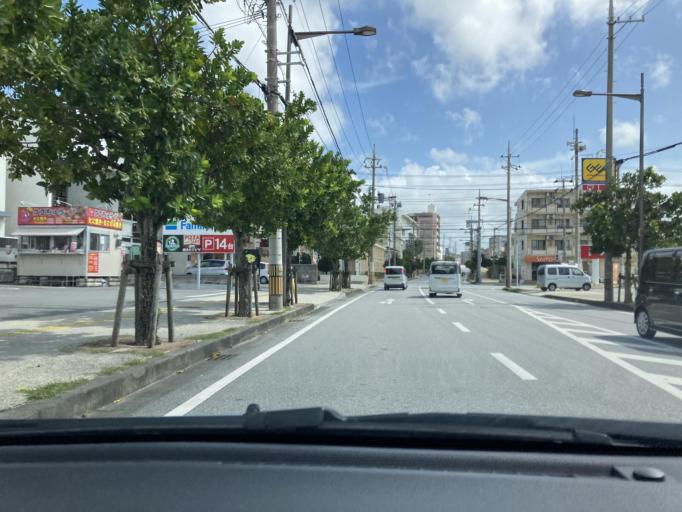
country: JP
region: Okinawa
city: Ginowan
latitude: 26.2735
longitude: 127.7298
